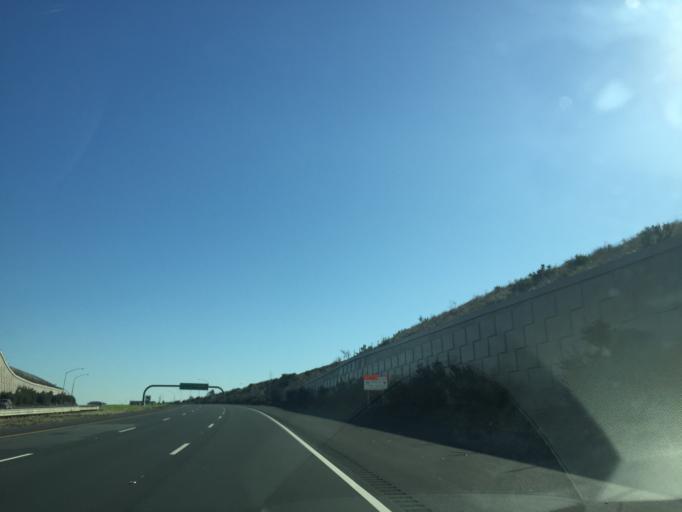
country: MX
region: Baja California
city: Tijuana
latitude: 32.5832
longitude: -116.9645
